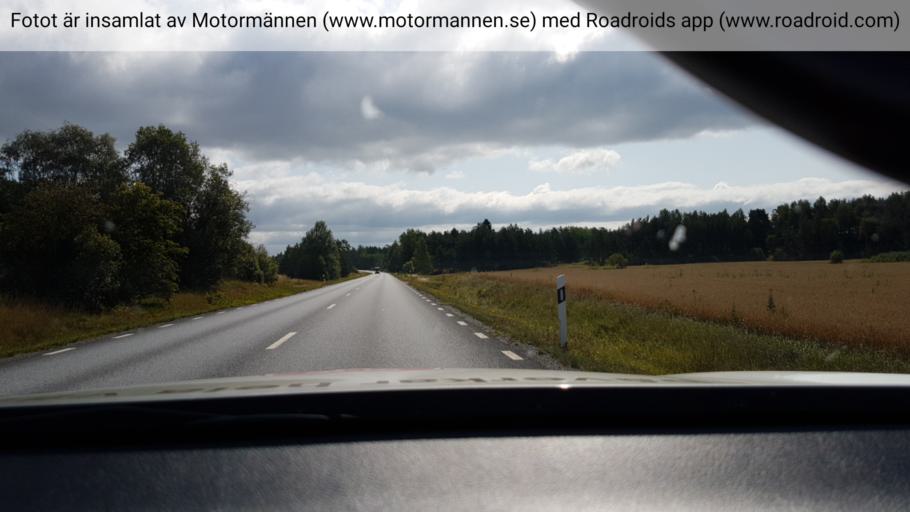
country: SE
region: Stockholm
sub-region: Vallentuna Kommun
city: Vallentuna
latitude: 59.7473
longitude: 18.0695
